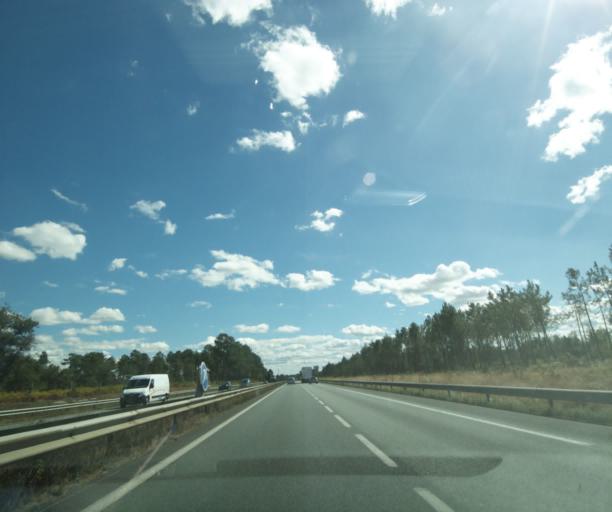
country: FR
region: Aquitaine
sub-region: Departement de la Gironde
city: Saint-Selve
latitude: 44.6518
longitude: -0.4431
